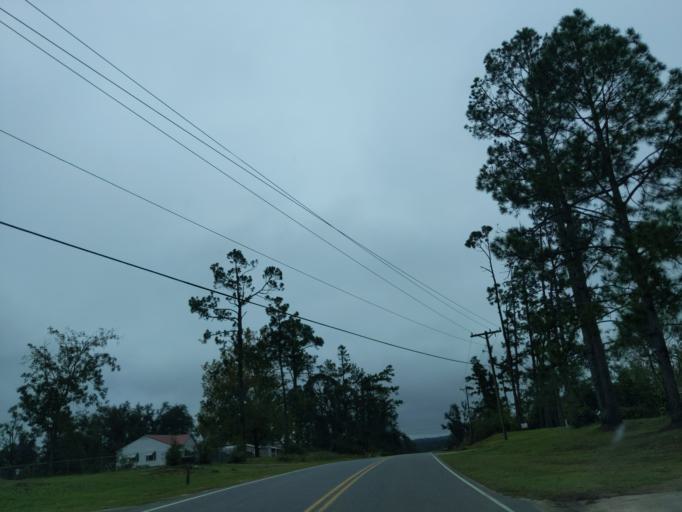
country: US
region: Florida
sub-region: Jackson County
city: Sneads
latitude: 30.7189
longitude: -84.9327
